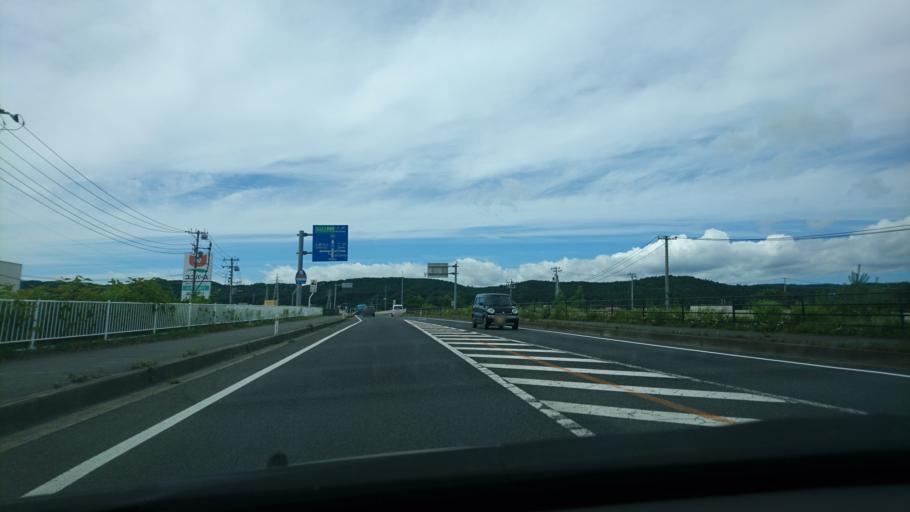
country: JP
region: Aomori
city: Hachinohe
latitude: 40.1918
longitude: 141.7860
